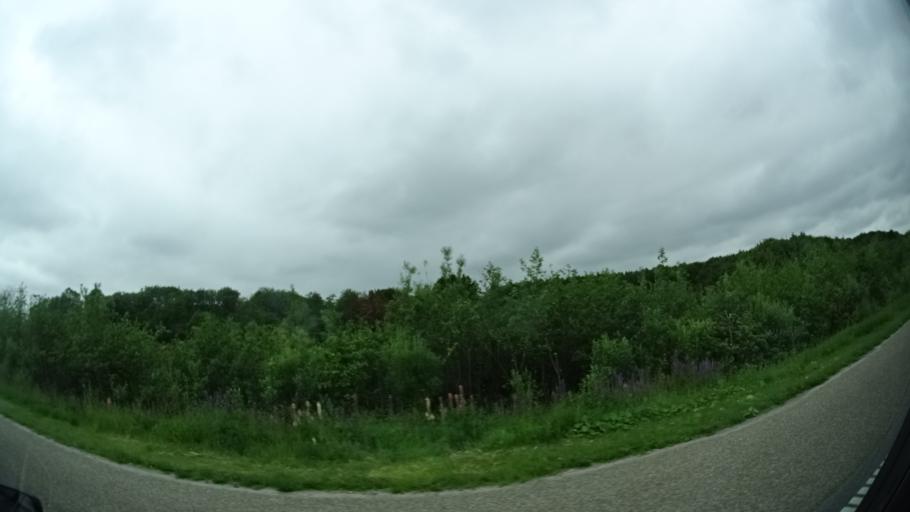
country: DK
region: Central Jutland
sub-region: Arhus Kommune
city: Hjortshoj
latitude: 56.2393
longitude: 10.2814
